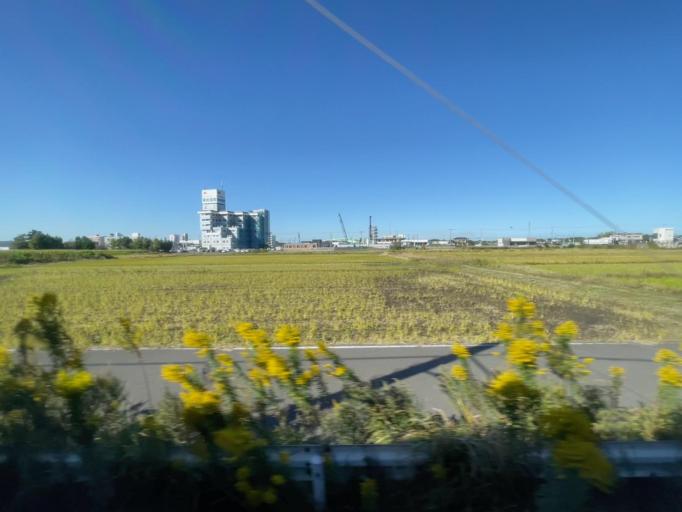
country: JP
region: Chiba
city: Asahi
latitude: 35.7244
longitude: 140.6650
